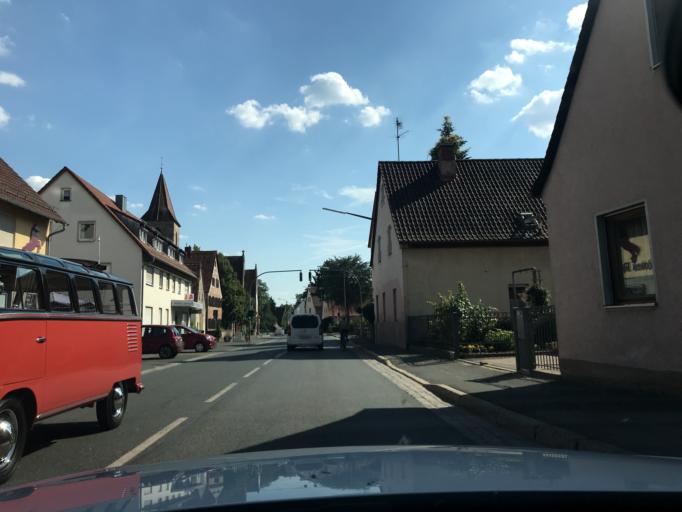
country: DE
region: Bavaria
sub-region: Regierungsbezirk Mittelfranken
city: Erlangen
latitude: 49.5548
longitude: 10.9886
